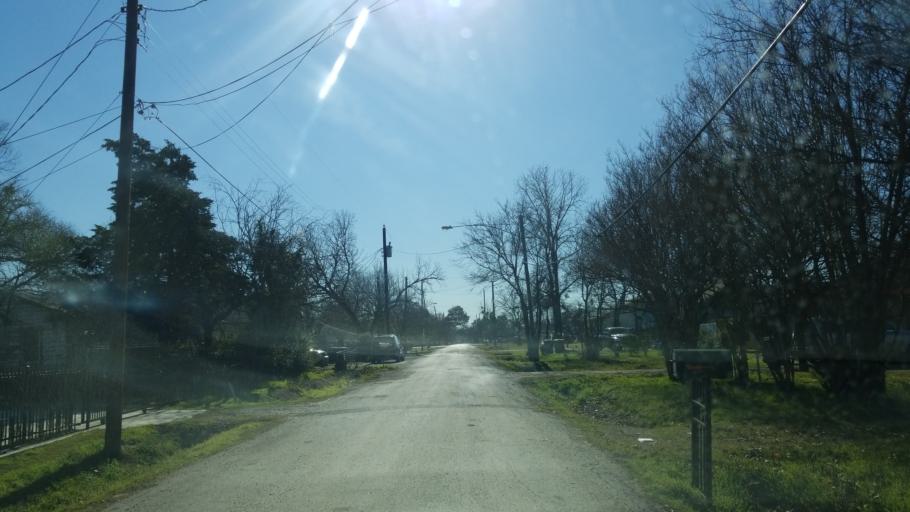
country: US
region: Texas
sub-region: Dallas County
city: Cockrell Hill
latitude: 32.7539
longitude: -96.9154
